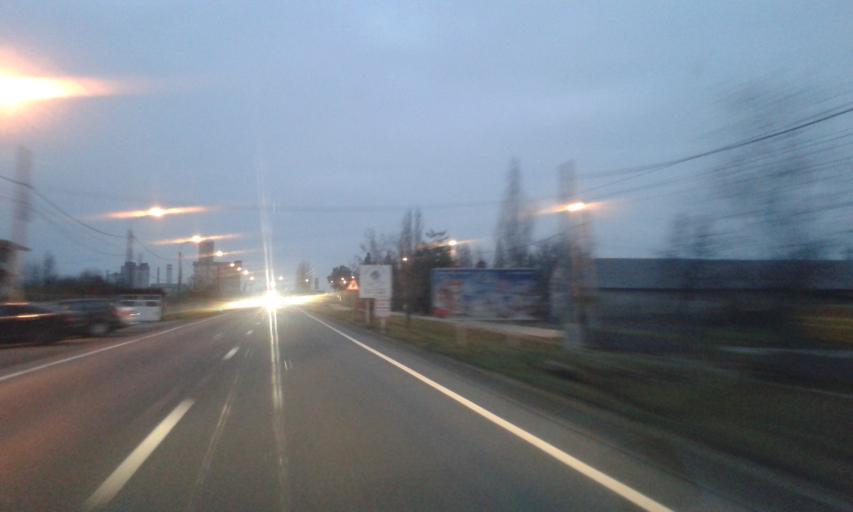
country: RO
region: Gorj
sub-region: Comuna Turcinesti
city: Turcinesti
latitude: 45.0798
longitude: 23.3132
